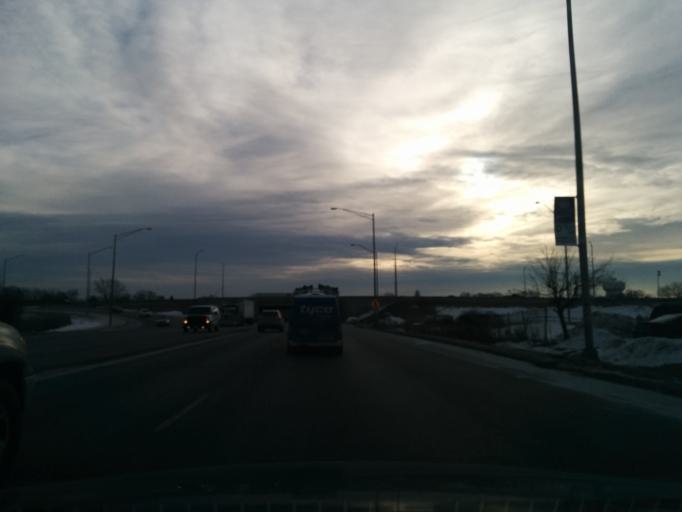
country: US
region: Illinois
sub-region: Cook County
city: Schiller Park
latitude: 41.9570
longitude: -87.8825
